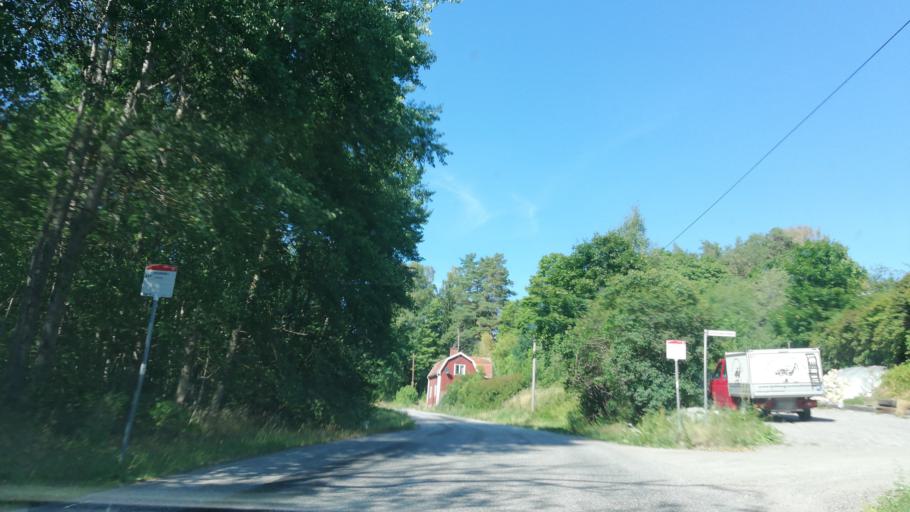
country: SE
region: OEstergoetland
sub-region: Finspangs Kommun
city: Finspang
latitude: 58.7229
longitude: 15.8324
